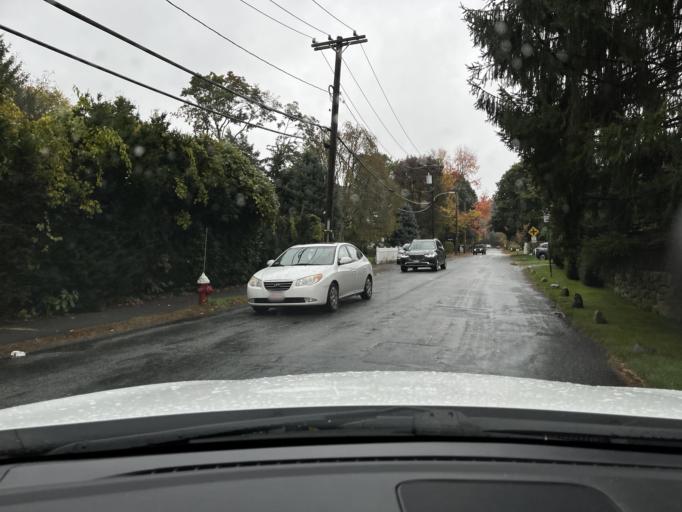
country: US
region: Massachusetts
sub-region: Norfolk County
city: Wellesley
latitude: 42.3008
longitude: -71.2838
